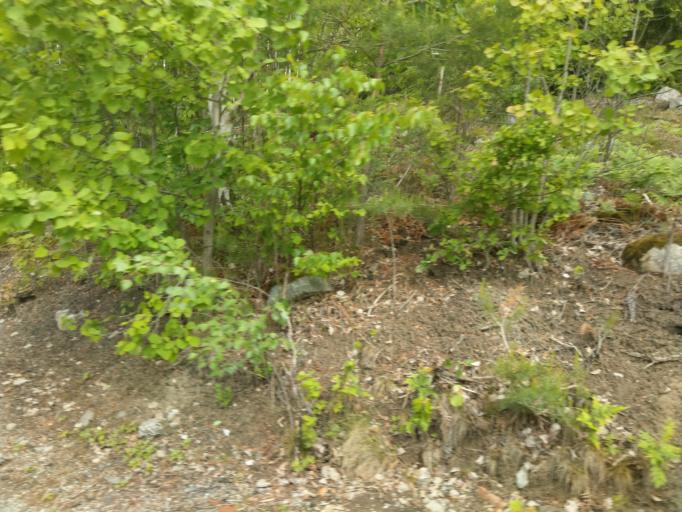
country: SE
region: Stockholm
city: Stenhamra
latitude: 59.4170
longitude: 17.6067
